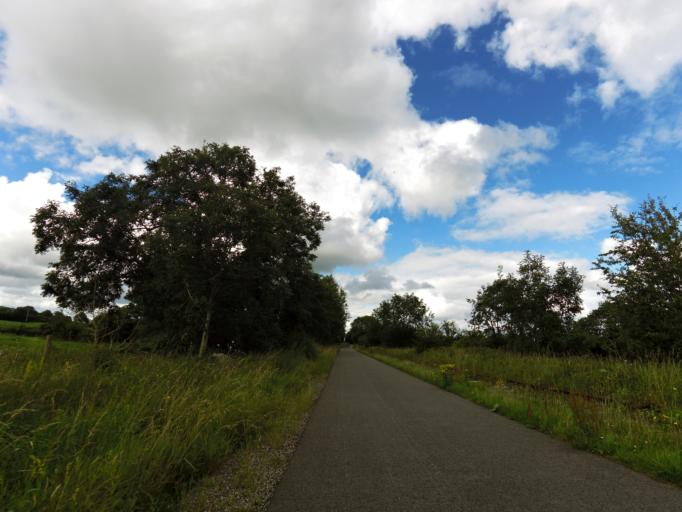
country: IE
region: Leinster
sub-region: An Iarmhi
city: Kilbeggan
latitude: 53.4586
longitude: -7.5151
